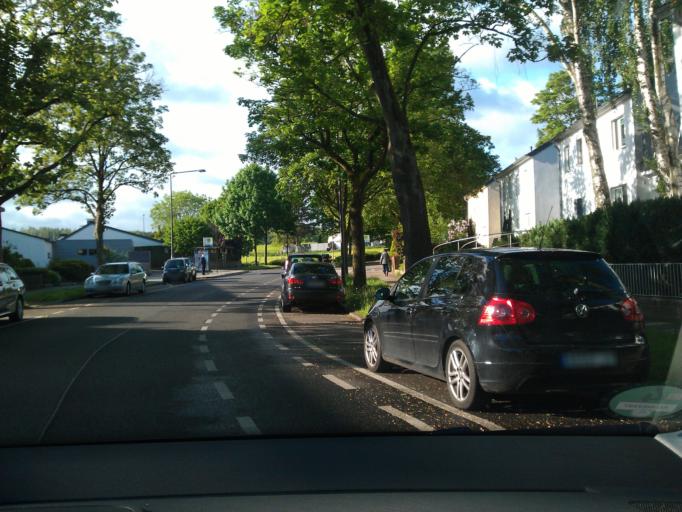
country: DE
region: North Rhine-Westphalia
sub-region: Regierungsbezirk Koln
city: Aachen
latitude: 50.7601
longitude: 6.1123
